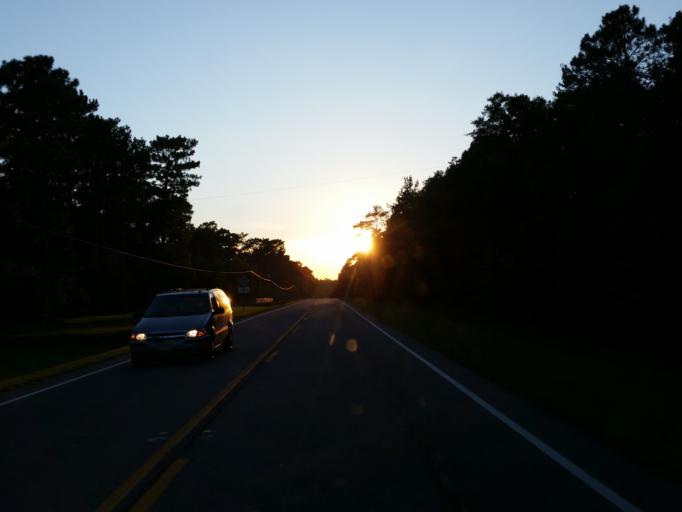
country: US
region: Georgia
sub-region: Berrien County
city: Nashville
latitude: 31.2173
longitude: -83.2788
